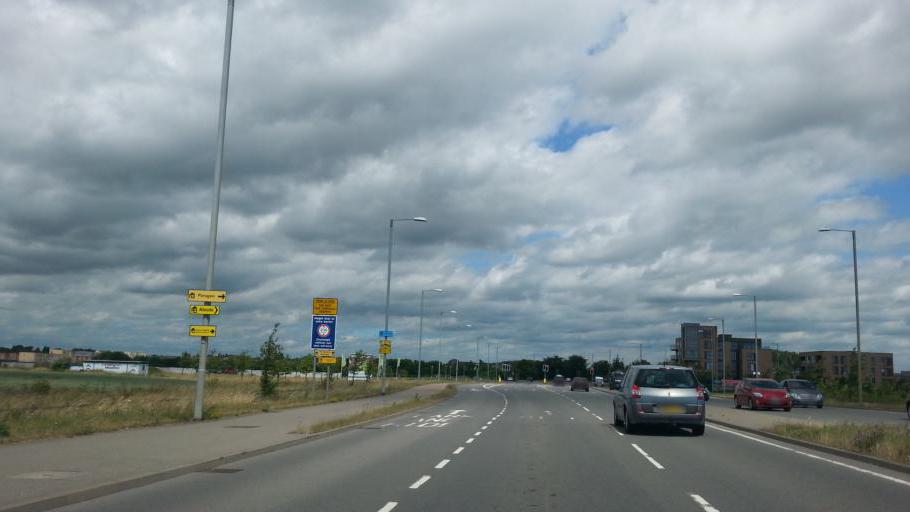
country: GB
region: England
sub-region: Cambridgeshire
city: Grantchester
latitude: 52.1631
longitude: 0.1064
